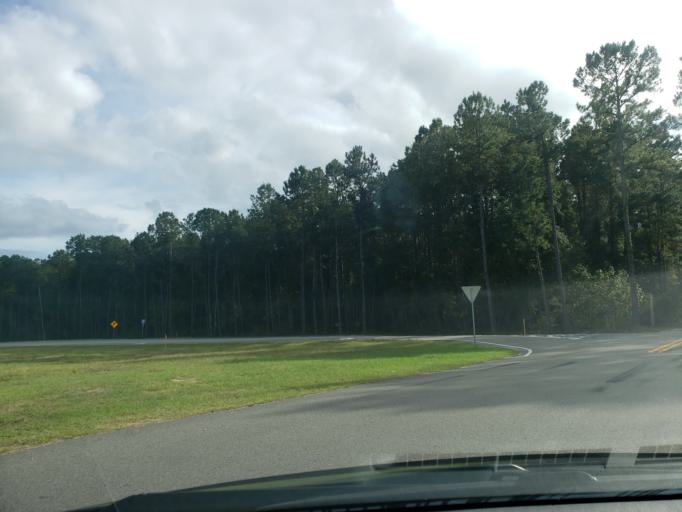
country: US
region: Georgia
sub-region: Bryan County
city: Richmond Hill
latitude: 32.0159
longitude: -81.3015
